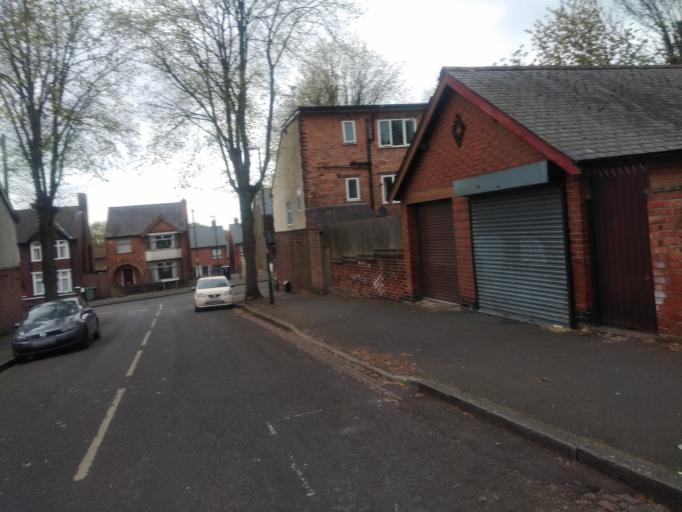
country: GB
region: England
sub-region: Nottingham
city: Nottingham
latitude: 52.9491
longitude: -1.1698
